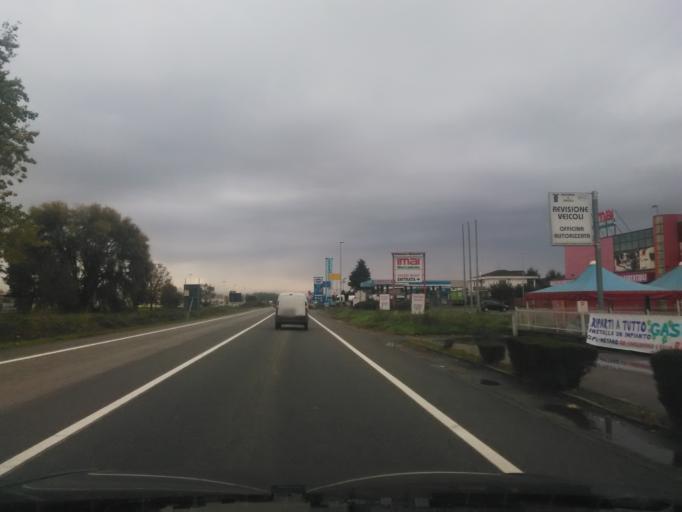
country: IT
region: Piedmont
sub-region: Provincia di Vercelli
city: Vercelli
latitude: 45.3223
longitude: 8.3897
